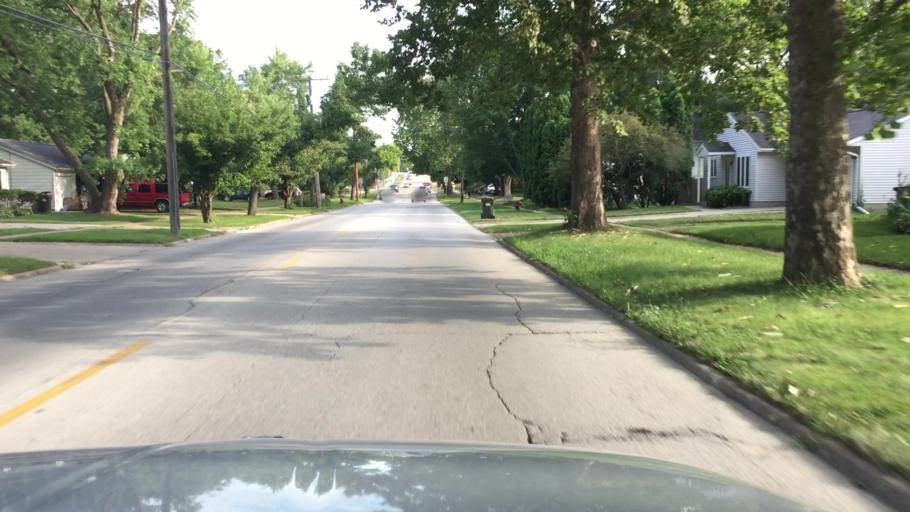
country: US
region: Iowa
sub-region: Johnson County
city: Iowa City
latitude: 41.6536
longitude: -91.5021
